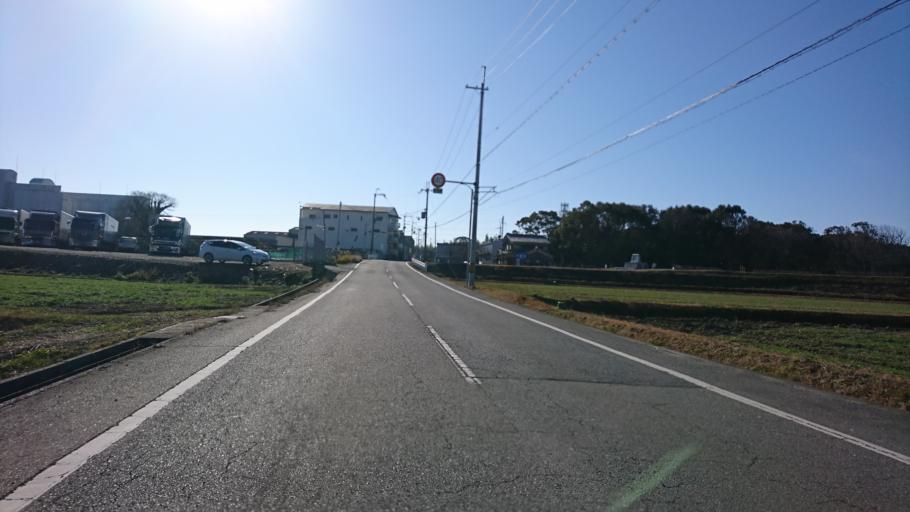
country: JP
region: Hyogo
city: Miki
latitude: 34.7564
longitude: 134.9256
